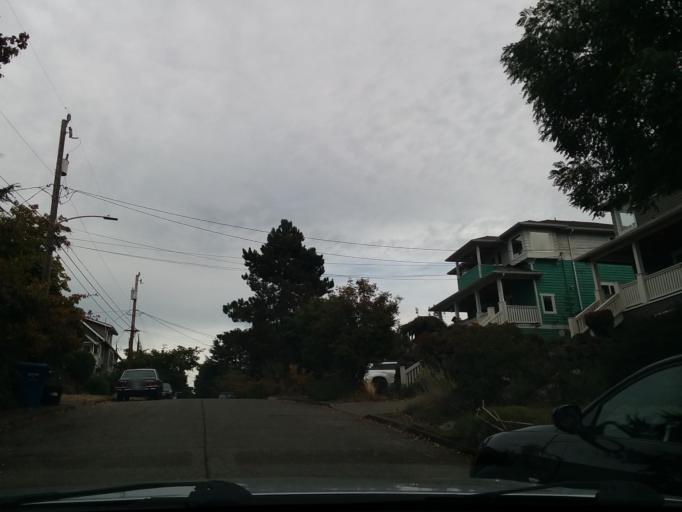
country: US
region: Washington
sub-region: King County
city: Seattle
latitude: 47.6556
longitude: -122.3584
